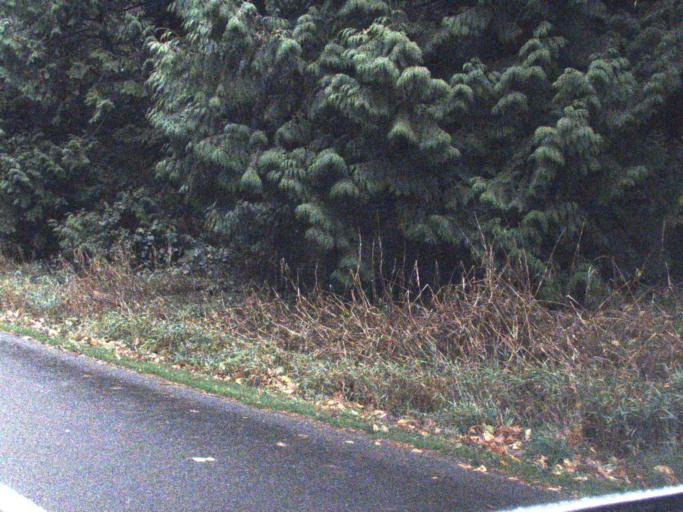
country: US
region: Washington
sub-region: Snohomish County
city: West Lake Stevens
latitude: 47.9712
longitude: -122.1024
